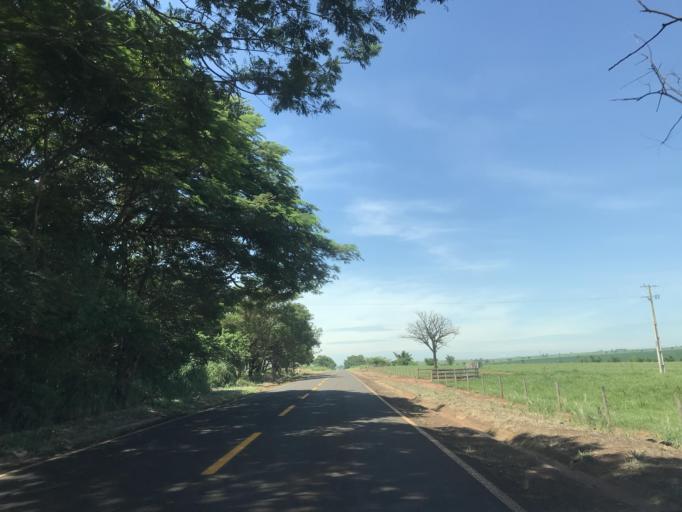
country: BR
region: Parana
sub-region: Terra Rica
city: Terra Rica
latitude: -22.7975
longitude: -52.6532
